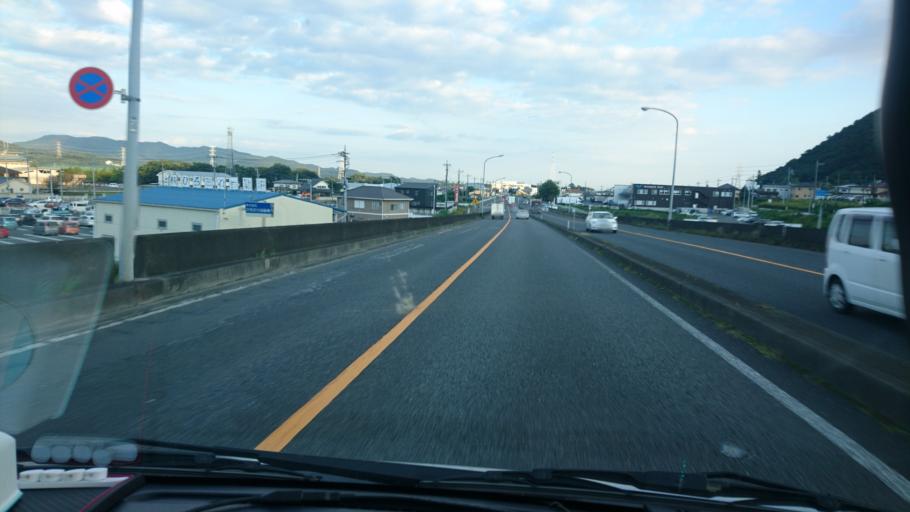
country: JP
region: Gunma
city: Kiryu
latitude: 36.3693
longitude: 139.3574
